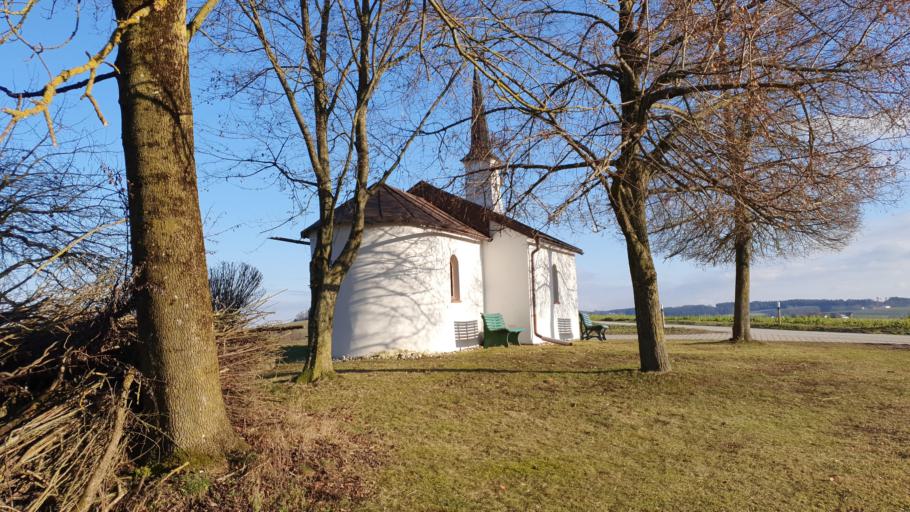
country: DE
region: Bavaria
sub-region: Lower Bavaria
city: Eichendorf
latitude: 48.6248
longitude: 12.8454
